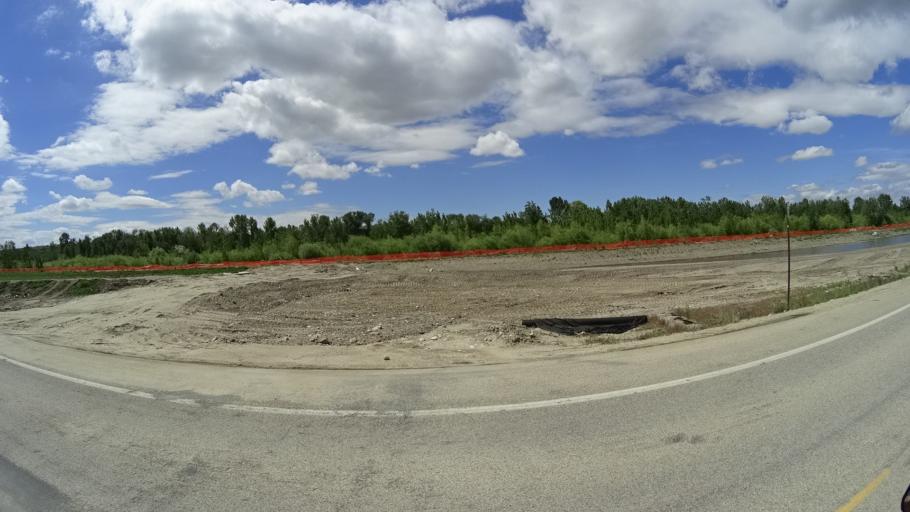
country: US
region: Idaho
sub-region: Ada County
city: Boise
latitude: 43.5718
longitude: -116.1358
